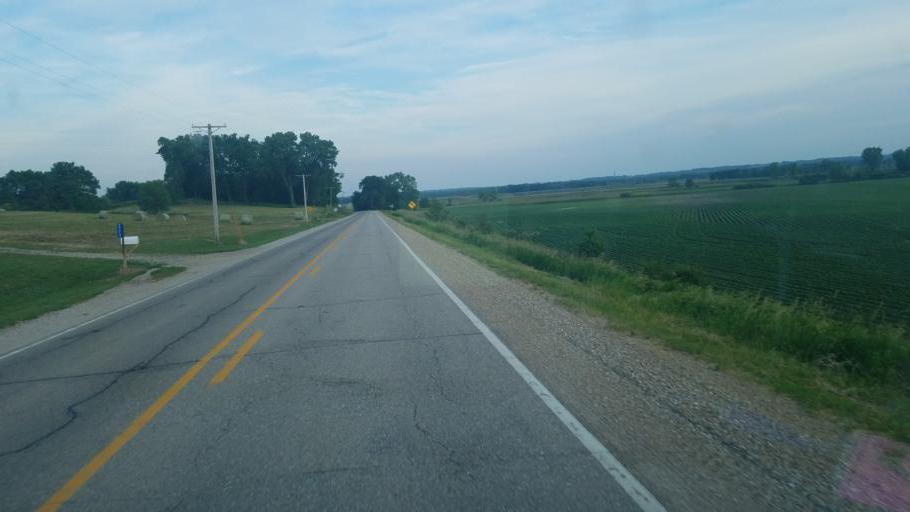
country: US
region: Iowa
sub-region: Tama County
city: Tama
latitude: 41.9540
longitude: -92.4227
